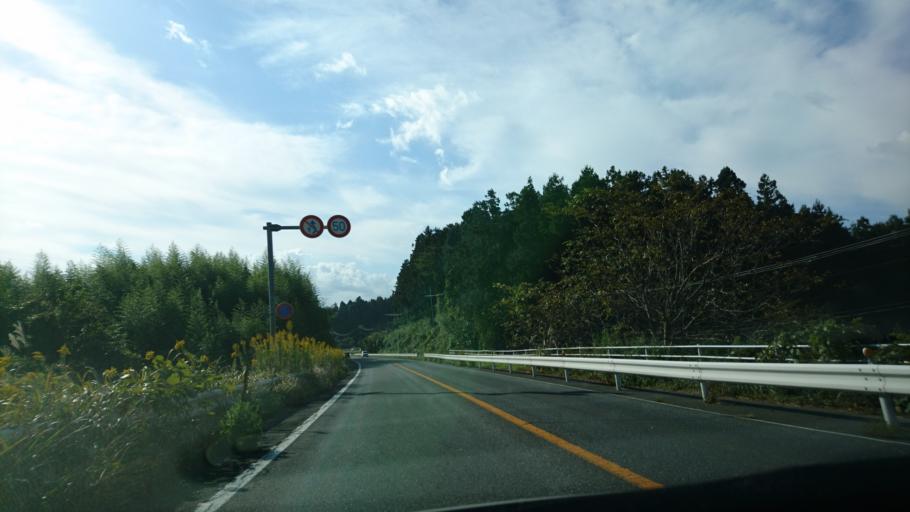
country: JP
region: Miyagi
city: Furukawa
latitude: 38.6270
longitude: 140.9823
